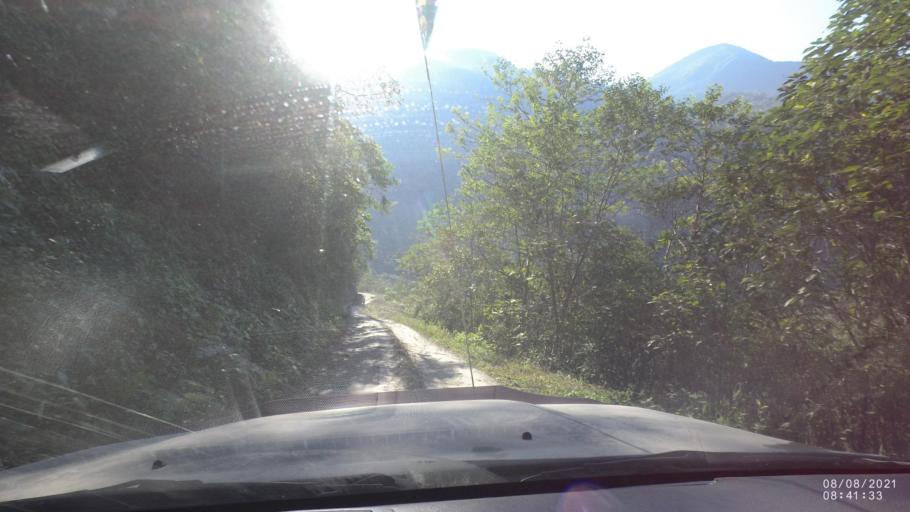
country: BO
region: La Paz
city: Quime
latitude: -16.5267
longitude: -66.7574
